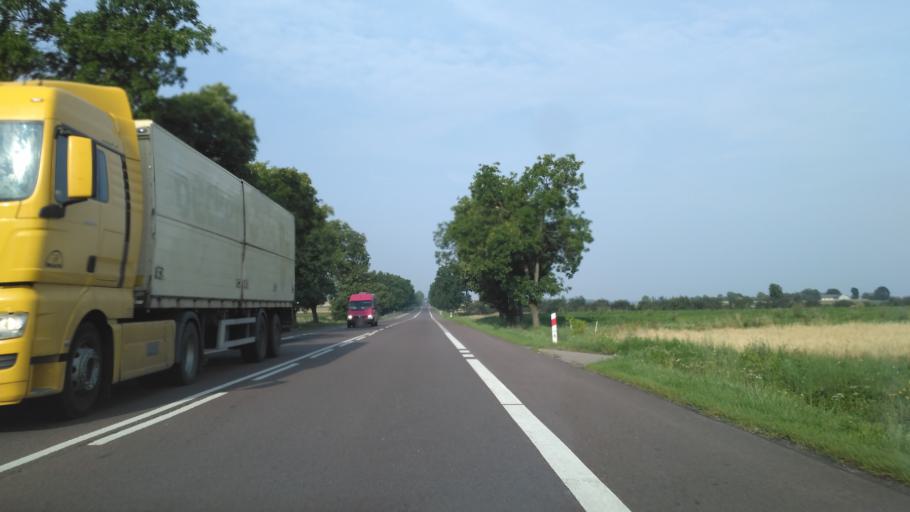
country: PL
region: Lublin Voivodeship
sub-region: Powiat chelmski
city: Rejowiec Fabryczny
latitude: 51.1723
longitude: 23.1349
